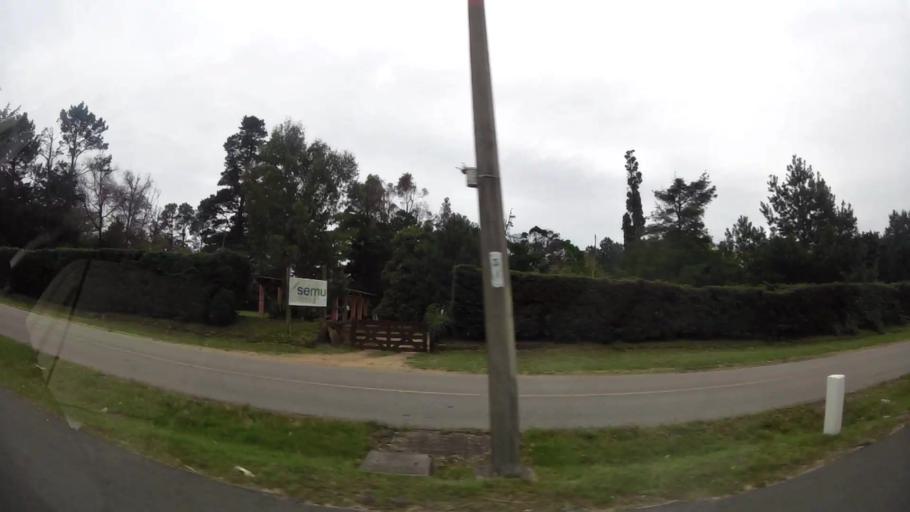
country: UY
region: Maldonado
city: Maldonado
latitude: -34.8786
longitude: -55.0542
